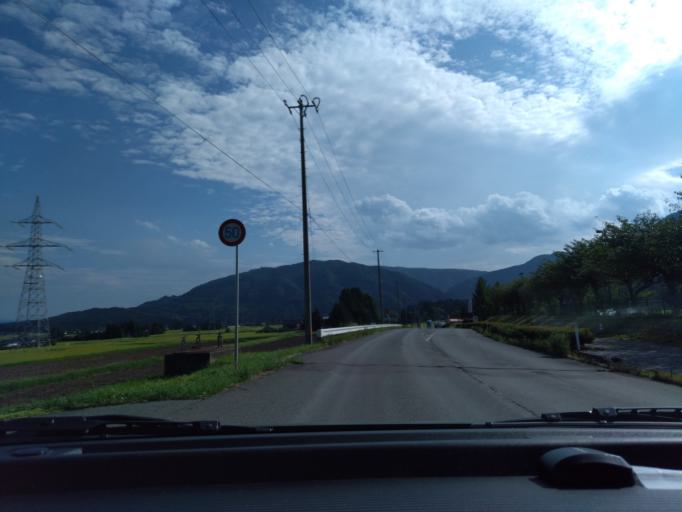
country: JP
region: Iwate
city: Morioka-shi
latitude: 39.5738
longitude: 141.0856
